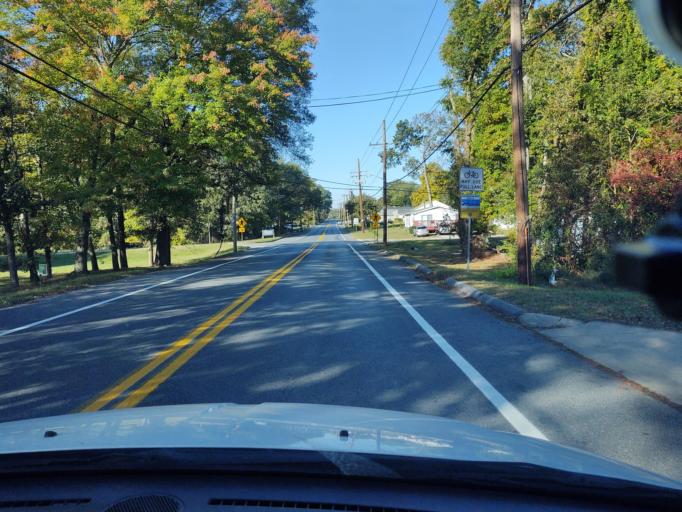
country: US
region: Maryland
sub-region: Prince George's County
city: Glenn Dale
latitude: 39.0069
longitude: -76.7723
